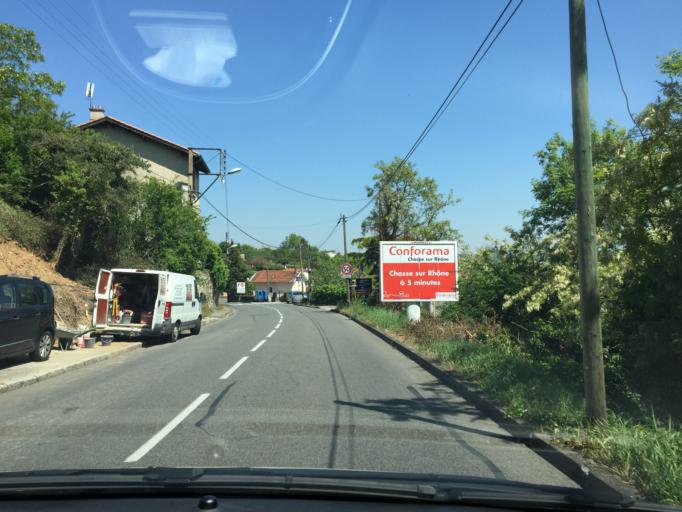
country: FR
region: Rhone-Alpes
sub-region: Departement du Rhone
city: Givors
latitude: 45.5870
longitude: 4.7532
